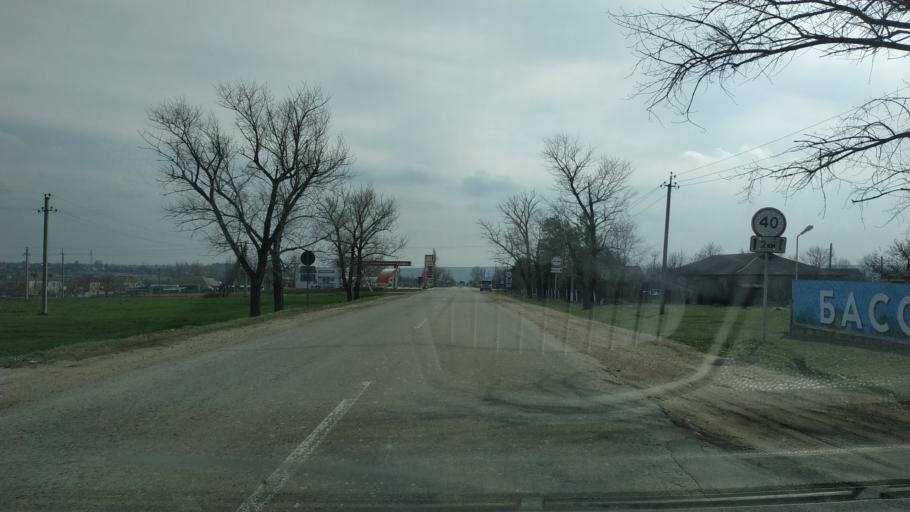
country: MD
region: Gagauzia
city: Vulcanesti
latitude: 45.6999
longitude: 28.4027
